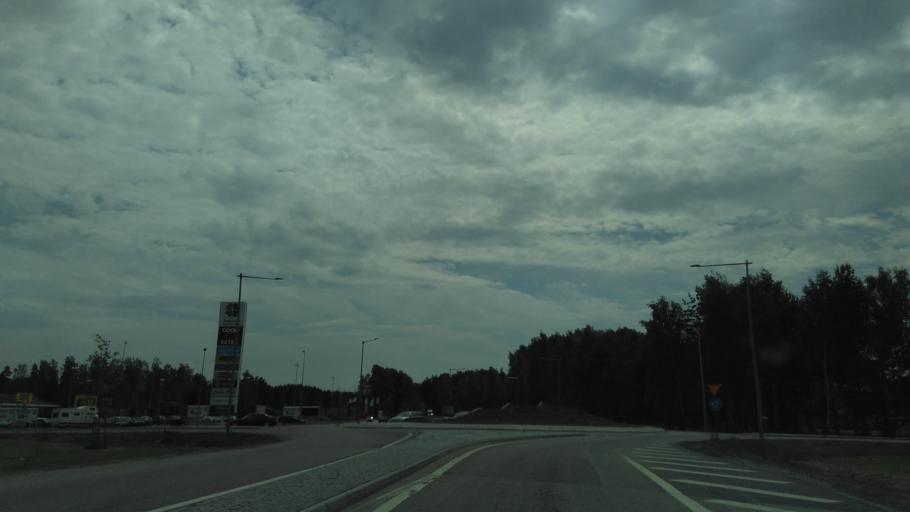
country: SE
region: Vaestra Goetaland
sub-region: Lidkopings Kommun
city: Lidkoping
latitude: 58.4946
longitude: 13.1817
